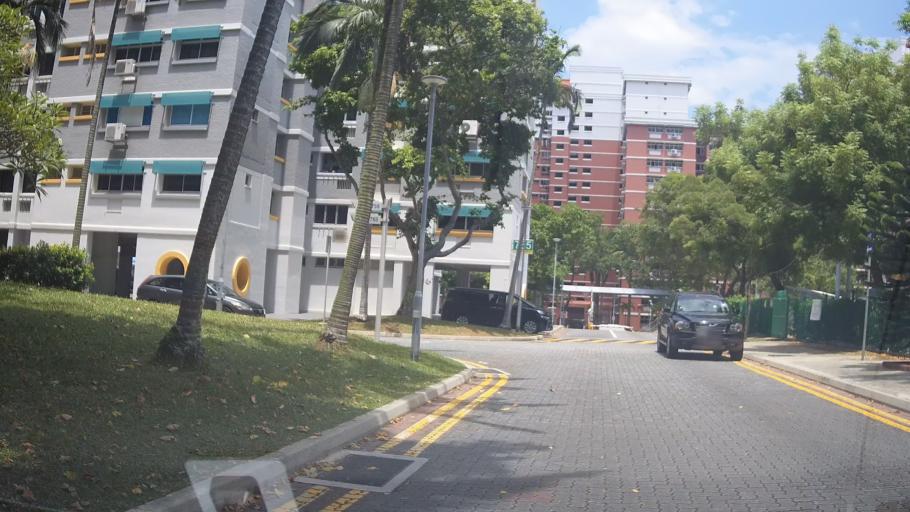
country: MY
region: Johor
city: Kampung Pasir Gudang Baru
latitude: 1.3763
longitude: 103.9347
